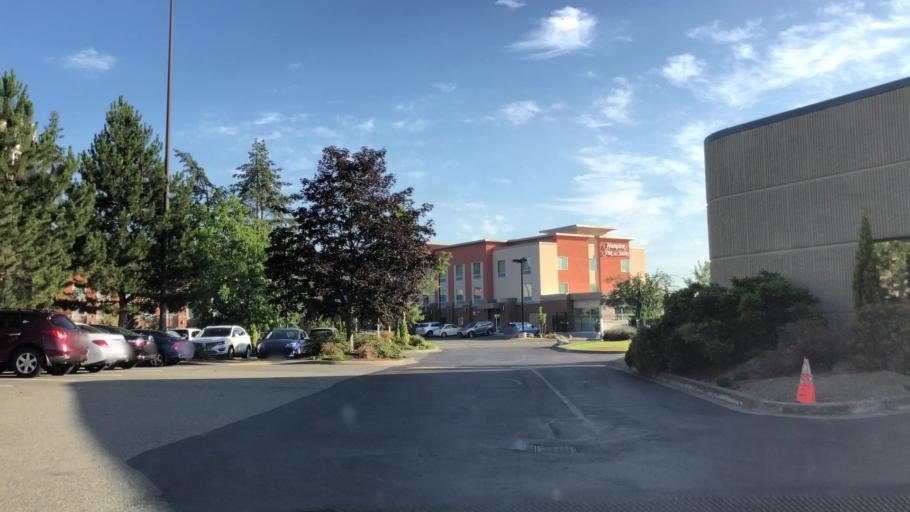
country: US
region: Washington
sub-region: King County
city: Redmond
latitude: 47.6729
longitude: -122.1026
